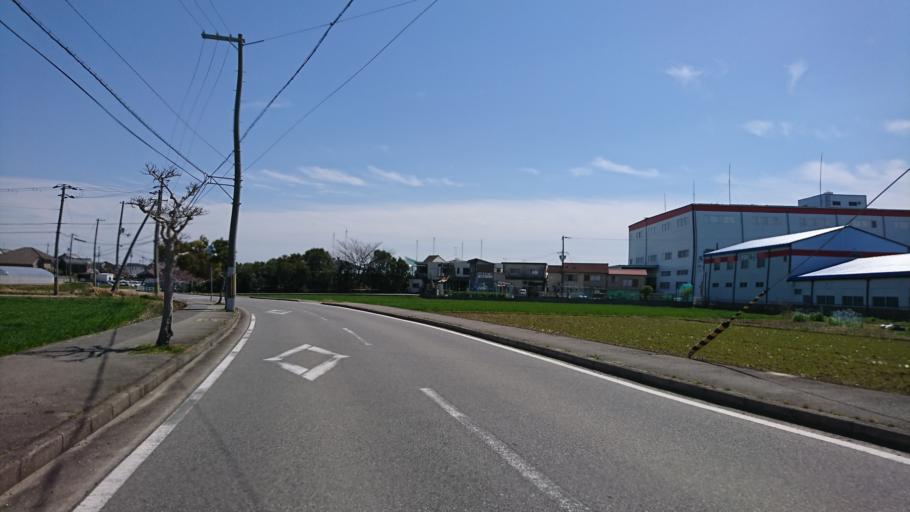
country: JP
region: Hyogo
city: Kakogawacho-honmachi
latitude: 34.7319
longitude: 134.9004
